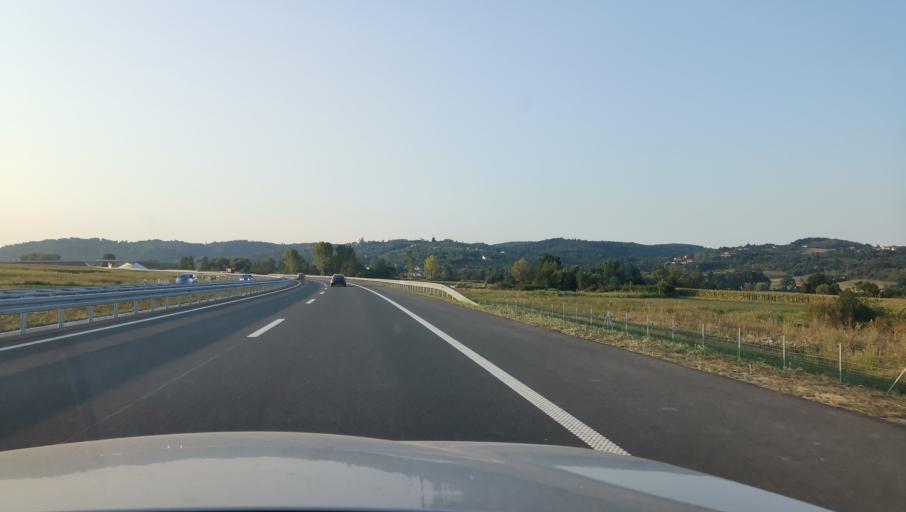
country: RS
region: Central Serbia
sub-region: Kolubarski Okrug
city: Lajkovac
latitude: 44.3254
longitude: 20.2128
